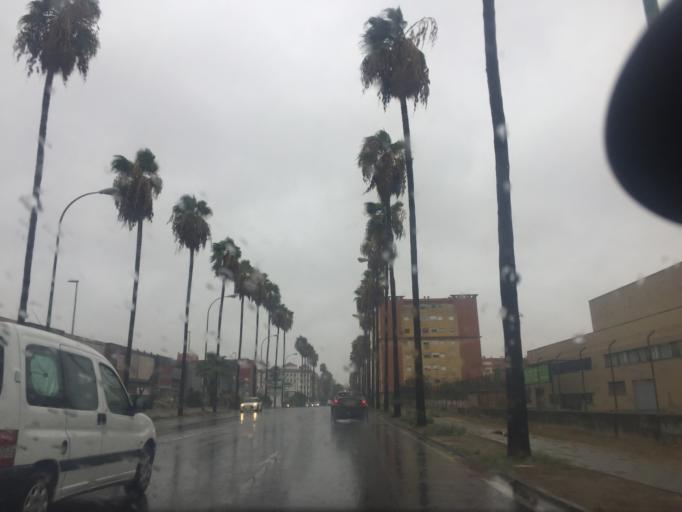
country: ES
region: Andalusia
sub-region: Provincia de Sevilla
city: Sevilla
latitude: 37.3654
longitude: -5.9556
